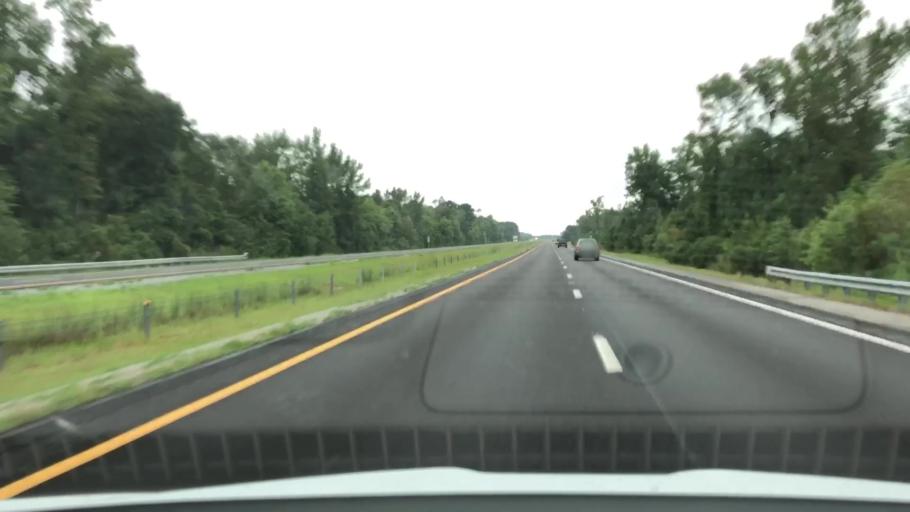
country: US
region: North Carolina
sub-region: Wayne County
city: Goldsboro
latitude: 35.4551
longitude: -77.9848
